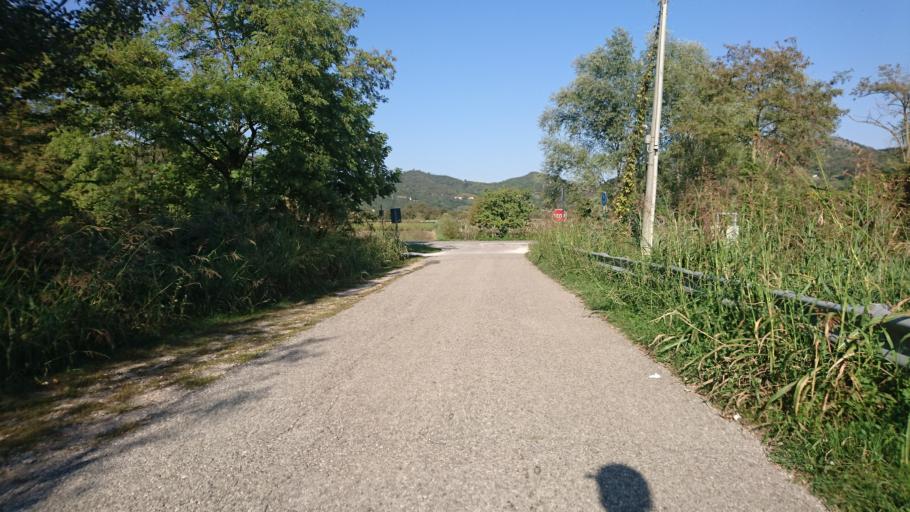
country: IT
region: Veneto
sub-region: Provincia di Padova
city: Galzignano
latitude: 45.3018
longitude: 11.7497
